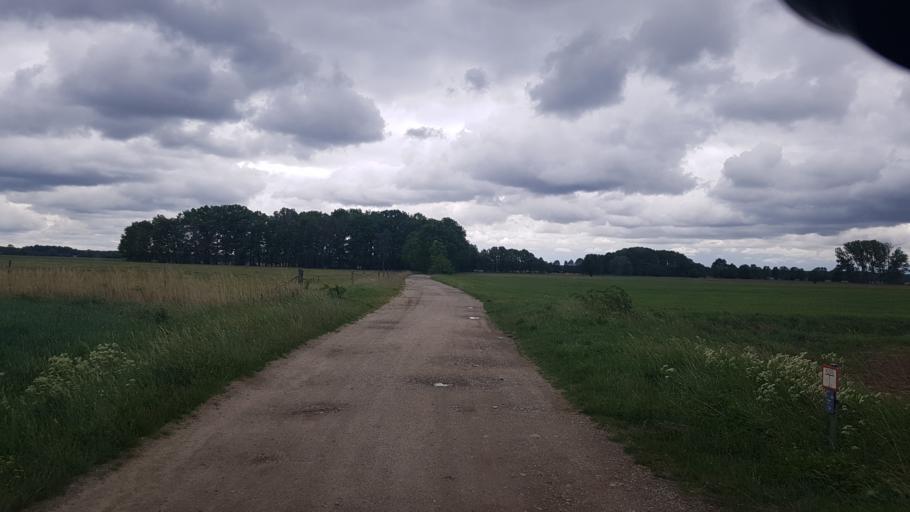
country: DE
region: Brandenburg
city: Ruckersdorf
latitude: 51.5817
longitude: 13.5429
